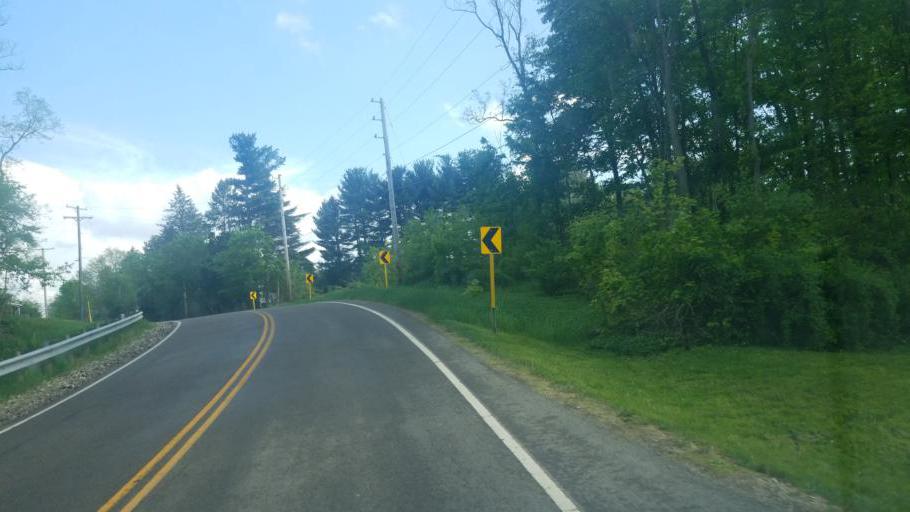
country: US
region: Ohio
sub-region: Ashland County
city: Ashland
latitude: 40.8787
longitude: -82.4169
